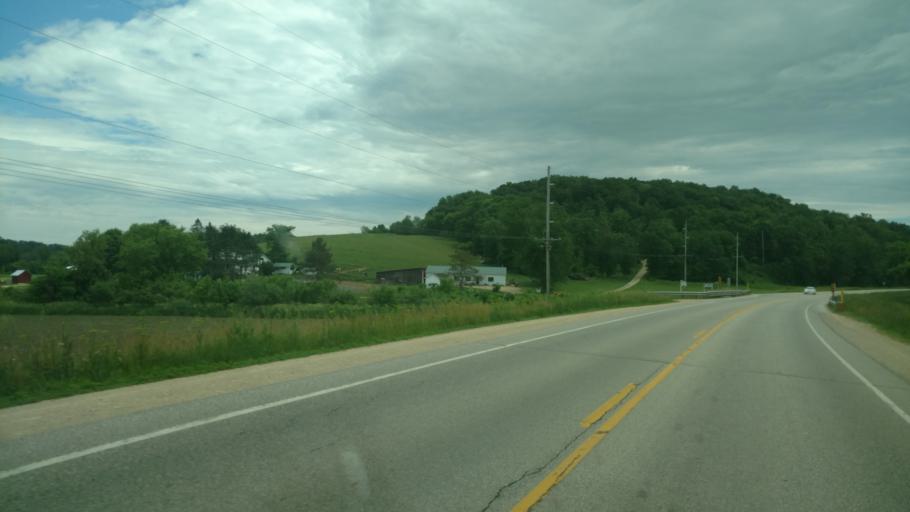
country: US
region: Wisconsin
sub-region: Monroe County
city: Tomah
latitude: 43.8240
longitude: -90.4453
